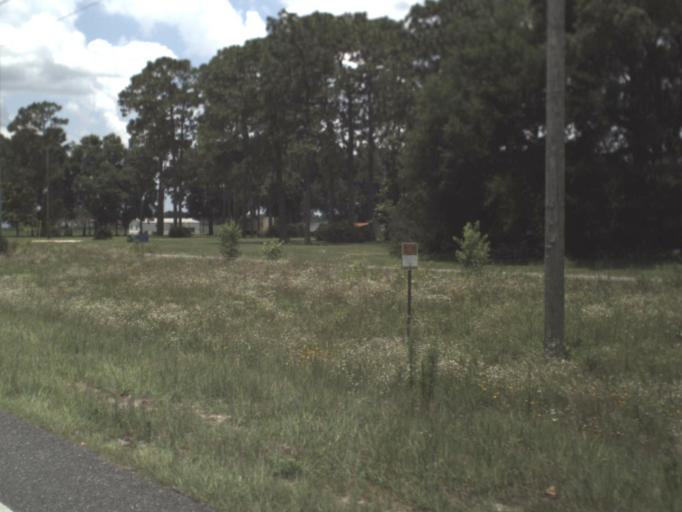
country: US
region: Florida
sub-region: Gilchrist County
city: Trenton
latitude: 29.6127
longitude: -82.8751
